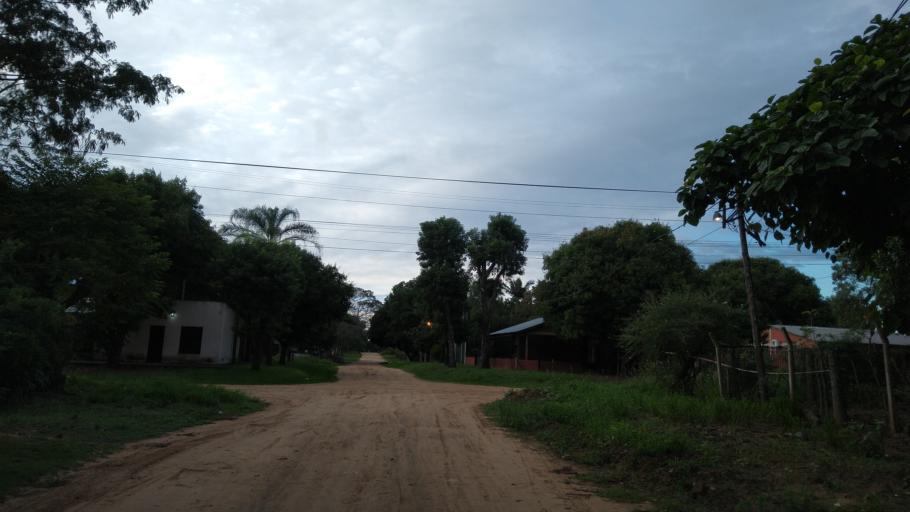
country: AR
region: Corrientes
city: Ituzaingo
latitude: -27.5911
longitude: -56.7052
